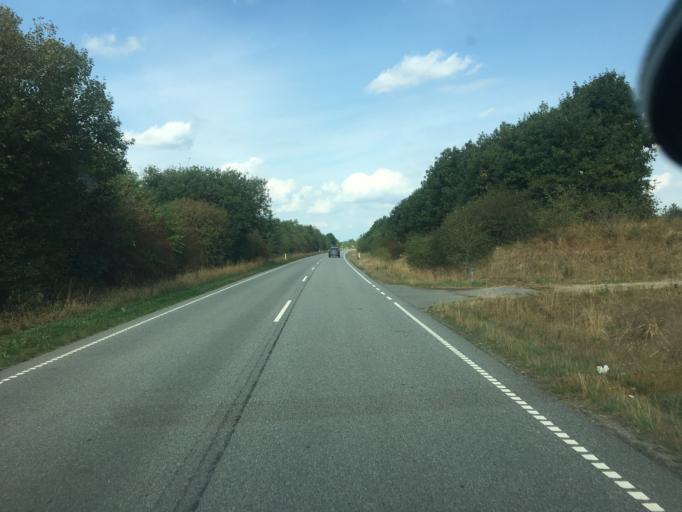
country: DK
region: South Denmark
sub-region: Aabenraa Kommune
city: Tinglev
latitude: 54.9424
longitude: 9.2917
